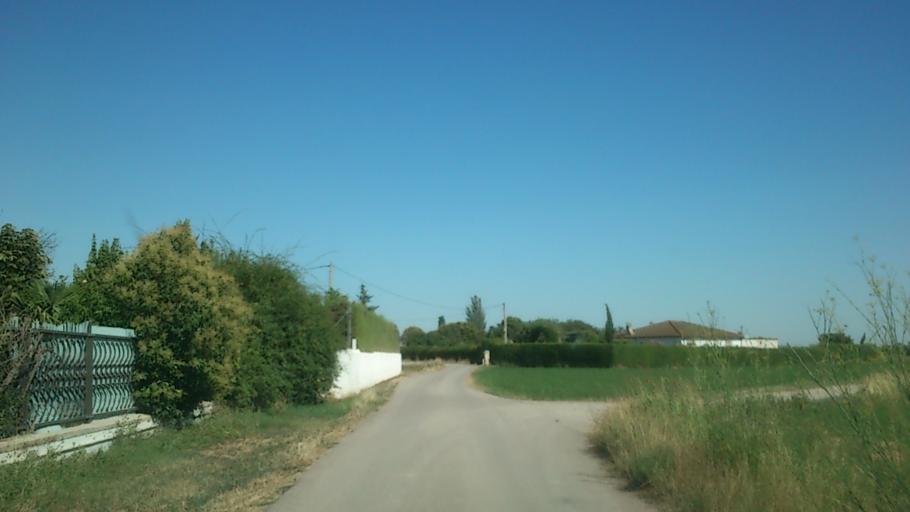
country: ES
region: Aragon
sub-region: Provincia de Zaragoza
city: Villanueva de Gallego
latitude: 41.6954
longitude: -0.8081
